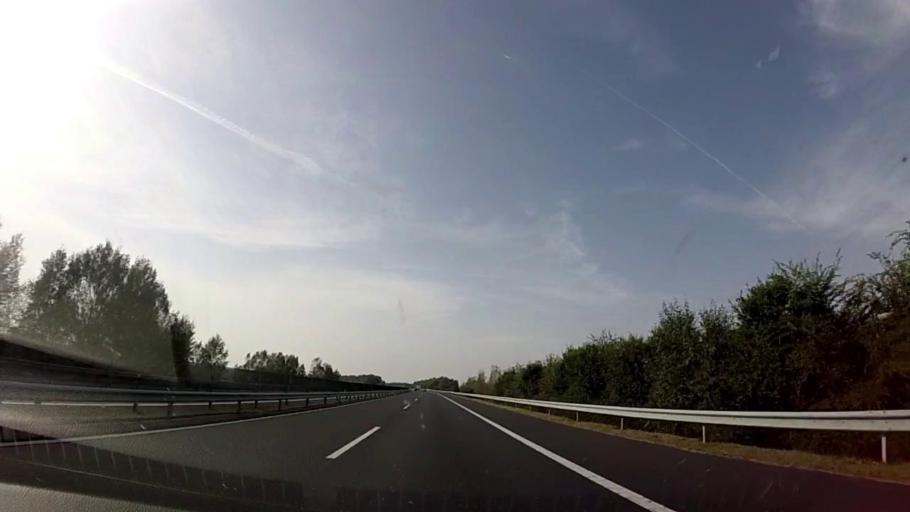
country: HU
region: Zala
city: Zalakomar
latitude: 46.5569
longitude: 17.2232
